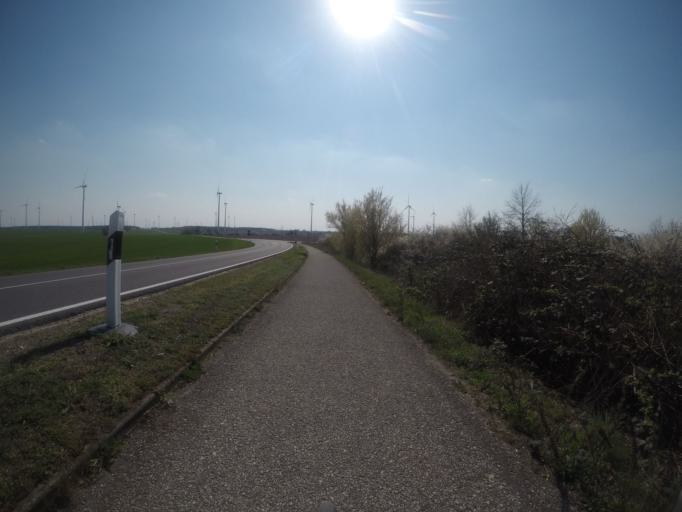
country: DE
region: Brandenburg
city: Nauen
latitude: 52.5558
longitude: 12.8686
